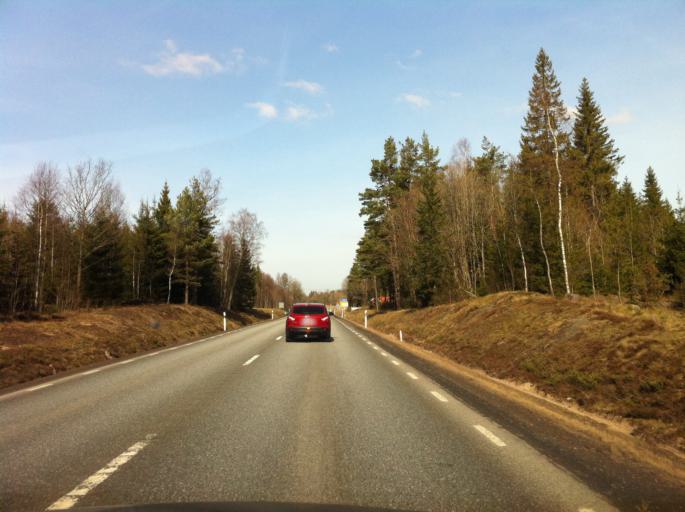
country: SE
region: Joenkoeping
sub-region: Mullsjo Kommun
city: Mullsjoe
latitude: 57.9881
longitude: 13.8285
